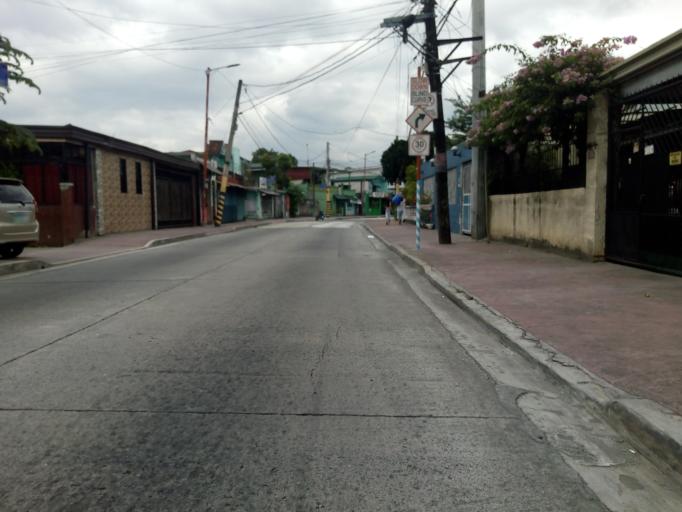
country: PH
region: Calabarzon
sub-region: Province of Rizal
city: Antipolo
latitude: 14.6374
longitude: 121.1180
